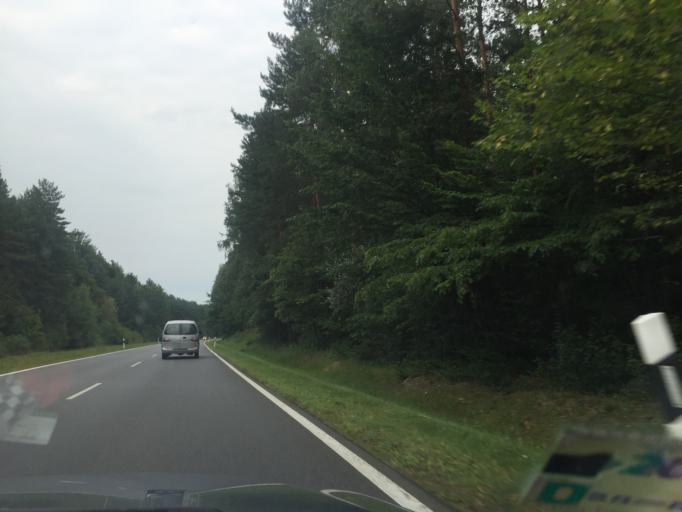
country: DE
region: Brandenburg
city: Wandlitz
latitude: 52.7291
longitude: 13.5249
